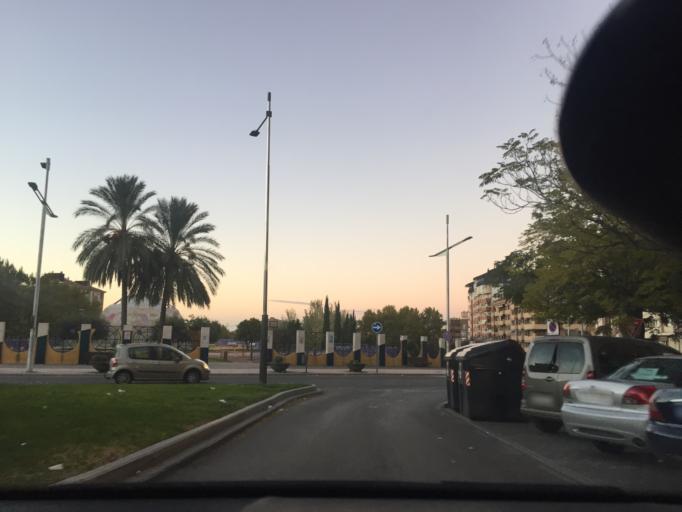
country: ES
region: Andalusia
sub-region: Provincia de Jaen
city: Jaen
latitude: 37.7806
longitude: -3.7896
